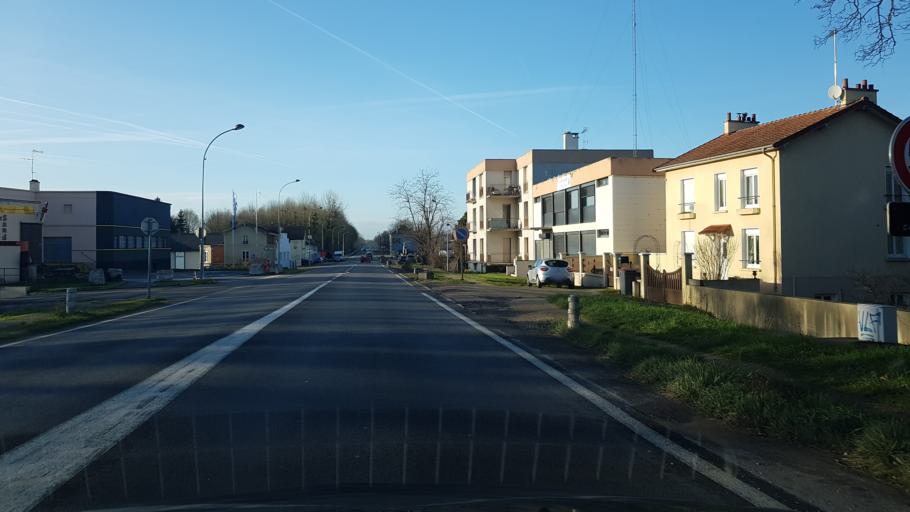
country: FR
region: Champagne-Ardenne
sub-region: Departement de la Marne
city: Vitry-le-Francois
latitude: 48.7285
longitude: 4.5767
